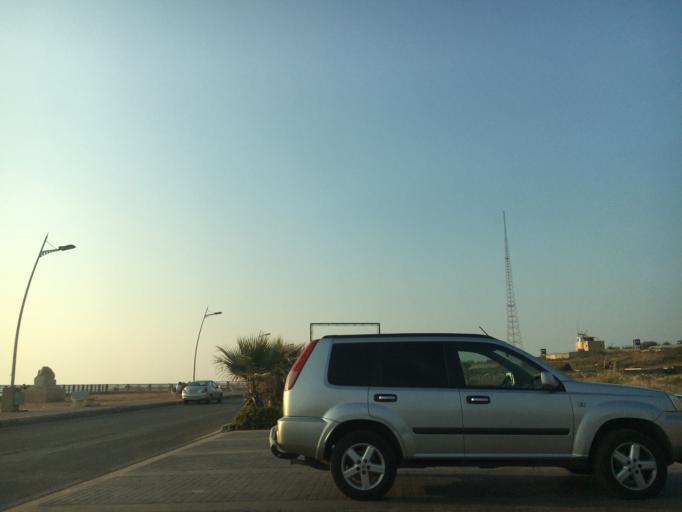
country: LB
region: Mont-Liban
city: Jbail
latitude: 34.1445
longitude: 35.6278
